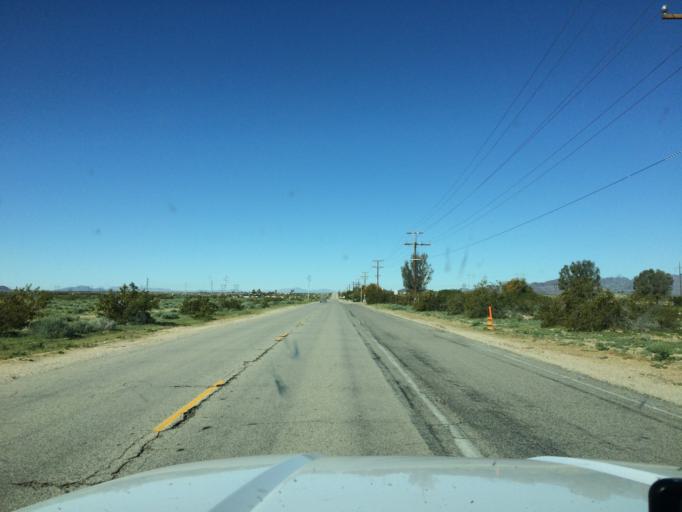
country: US
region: California
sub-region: Riverside County
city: Mesa Verde
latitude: 33.6100
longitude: -114.6816
